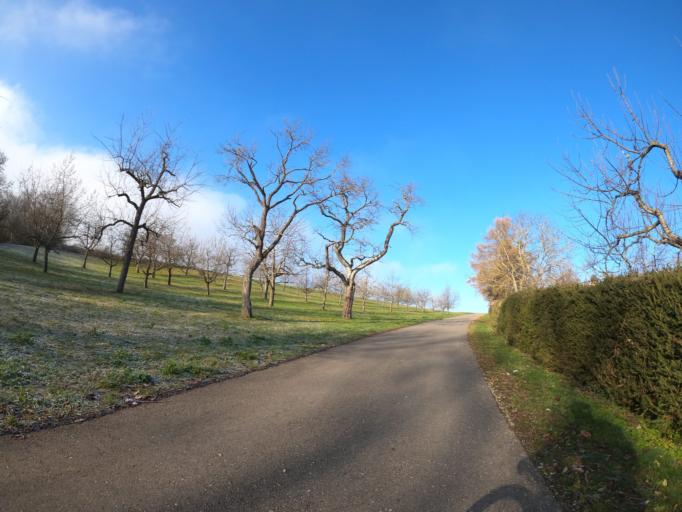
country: DE
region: Baden-Wuerttemberg
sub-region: Regierungsbezirk Stuttgart
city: Bad Uberkingen
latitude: 48.5850
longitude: 9.7953
